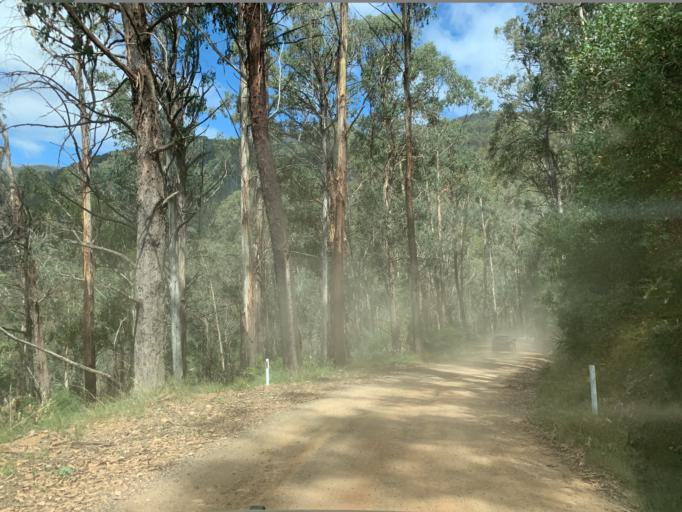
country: AU
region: Victoria
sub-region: Mansfield
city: Mansfield
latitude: -37.1012
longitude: 146.4993
